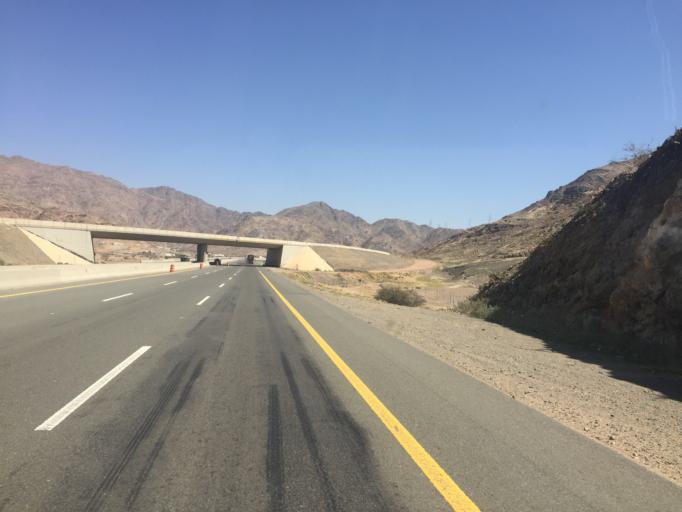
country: SA
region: Al Madinah al Munawwarah
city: Badr Hunayn
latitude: 24.0900
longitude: 39.1047
